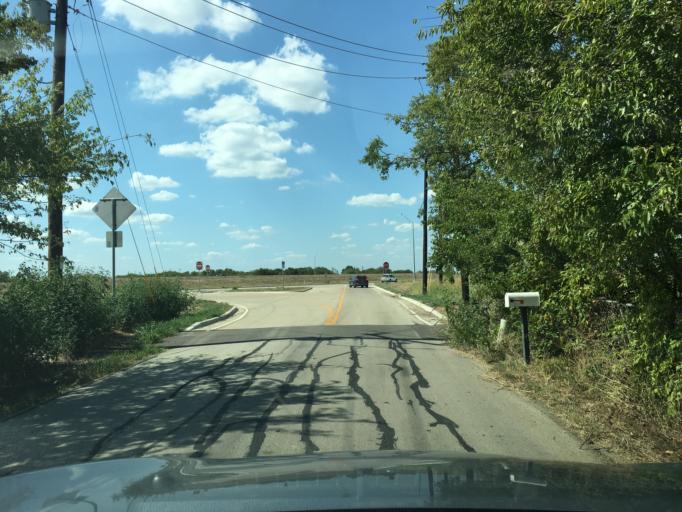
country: US
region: Texas
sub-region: Tarrant County
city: Mansfield
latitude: 32.5265
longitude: -97.0807
